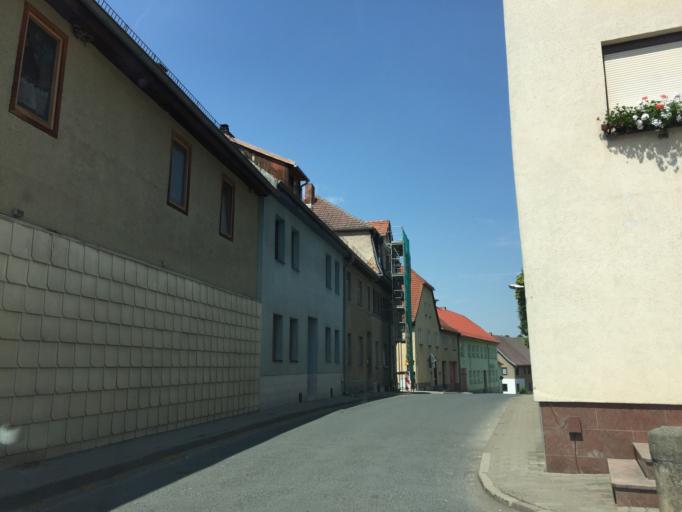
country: DE
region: Thuringia
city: Rittersdorf
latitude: 50.7595
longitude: 11.2280
